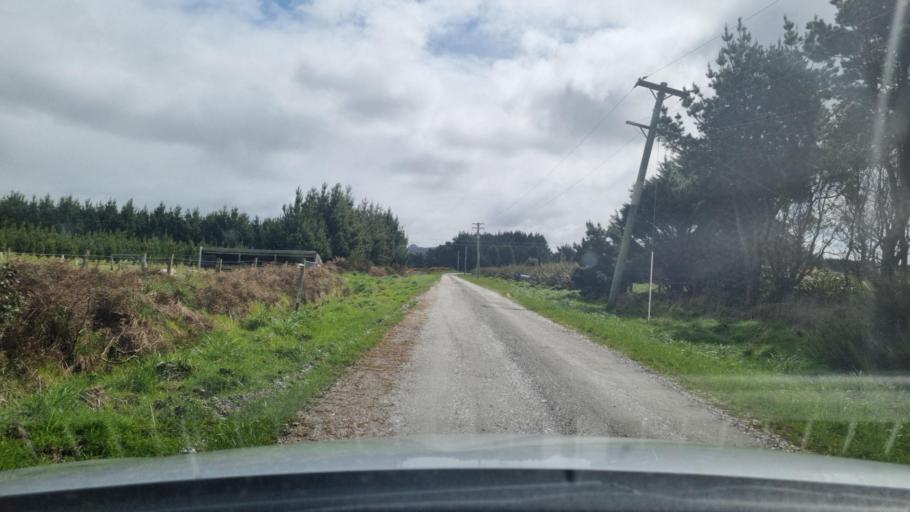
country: NZ
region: Southland
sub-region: Invercargill City
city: Bluff
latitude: -46.5393
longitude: 168.3021
